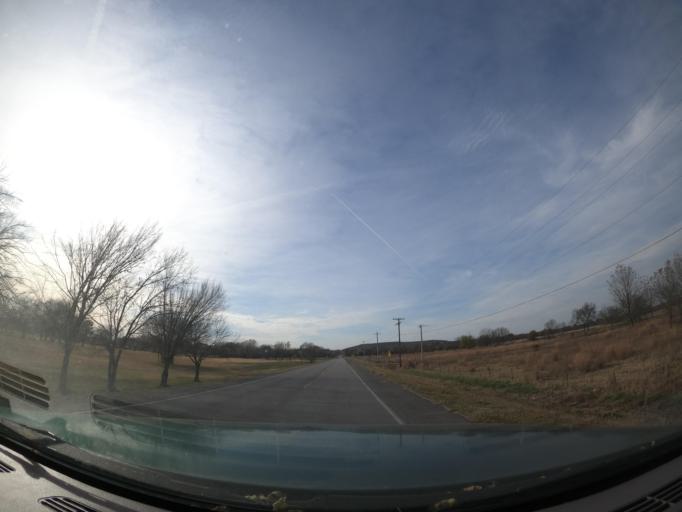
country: US
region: Oklahoma
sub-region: Tulsa County
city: Turley
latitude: 36.2496
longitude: -95.9551
